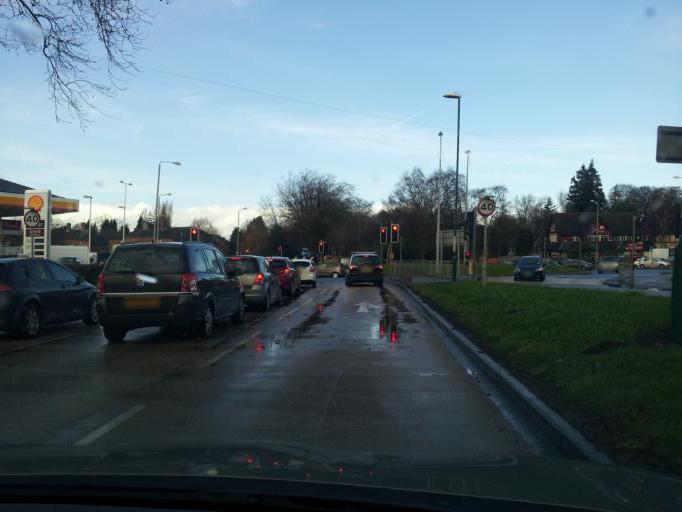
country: GB
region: England
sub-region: Nottingham
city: Nottingham
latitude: 52.9383
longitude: -1.2162
